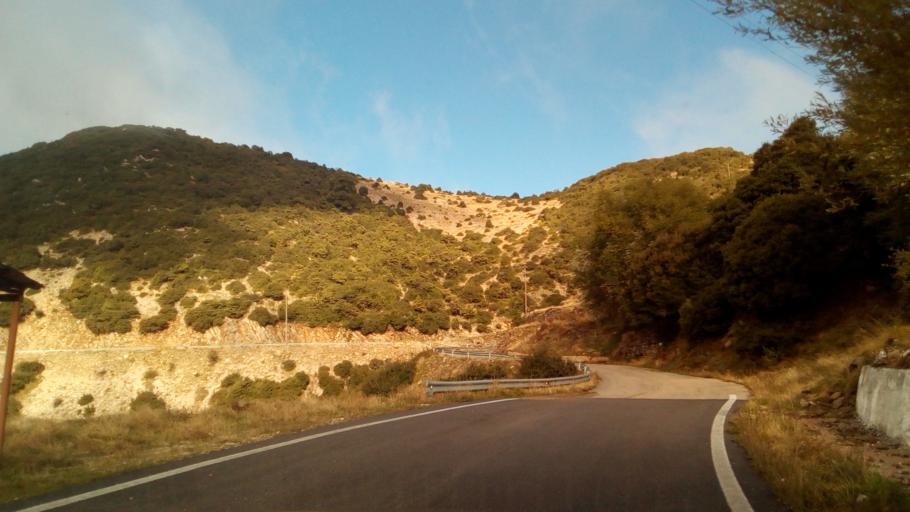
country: GR
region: West Greece
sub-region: Nomos Aitolias kai Akarnanias
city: Thermo
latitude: 38.5870
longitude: 21.7715
